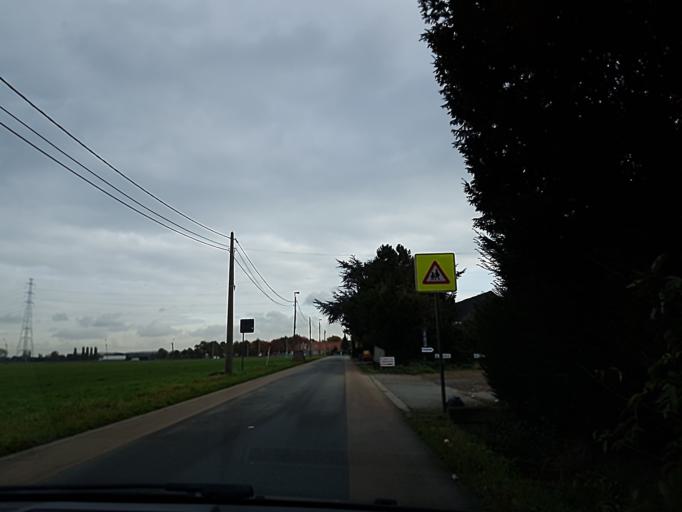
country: BE
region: Flanders
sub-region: Provincie Antwerpen
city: Ranst
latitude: 51.1731
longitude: 4.5594
